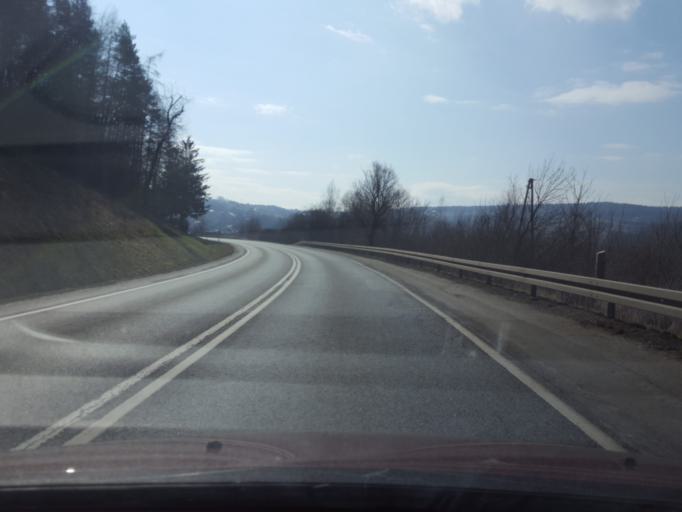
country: PL
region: Lesser Poland Voivodeship
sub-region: Powiat nowosadecki
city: Chelmiec
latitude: 49.6798
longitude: 20.6531
